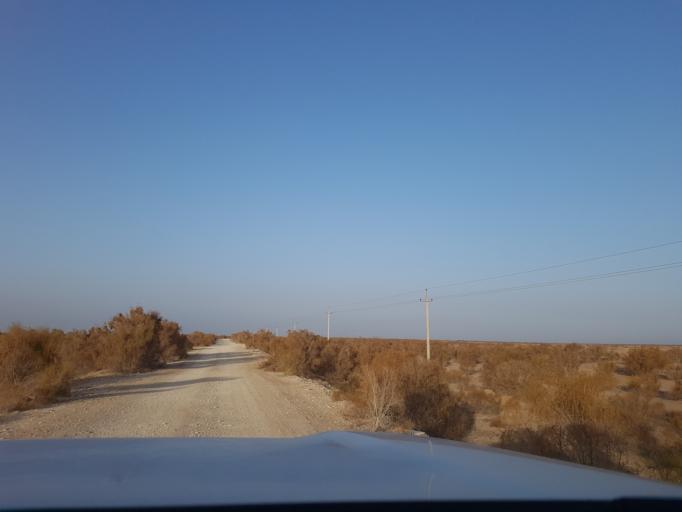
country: TM
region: Dasoguz
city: Koeneuergench
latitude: 41.8534
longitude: 58.2494
